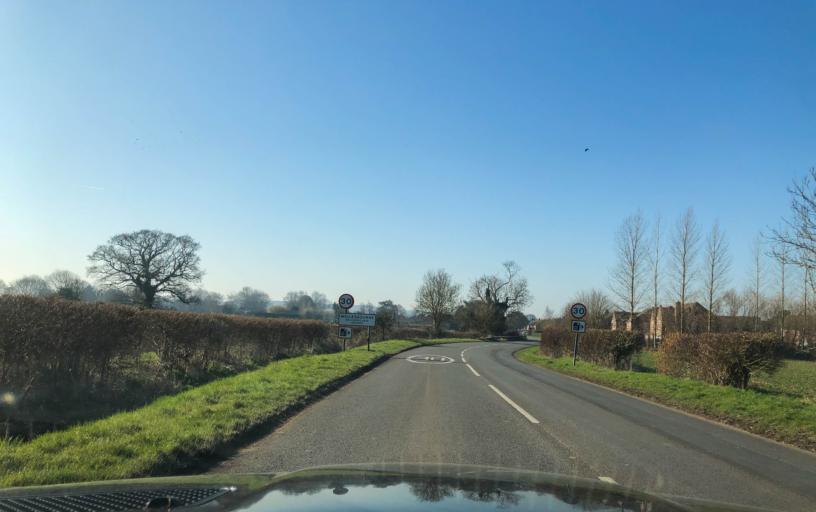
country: GB
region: England
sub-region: Warwickshire
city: Wellesbourne Mountford
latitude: 52.2012
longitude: -1.5855
